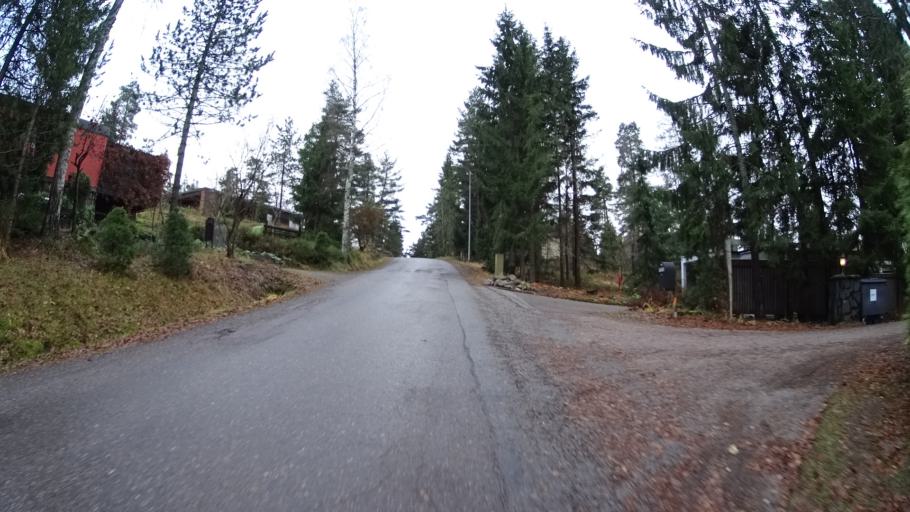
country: FI
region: Uusimaa
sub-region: Helsinki
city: Kauniainen
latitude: 60.2172
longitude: 24.7351
